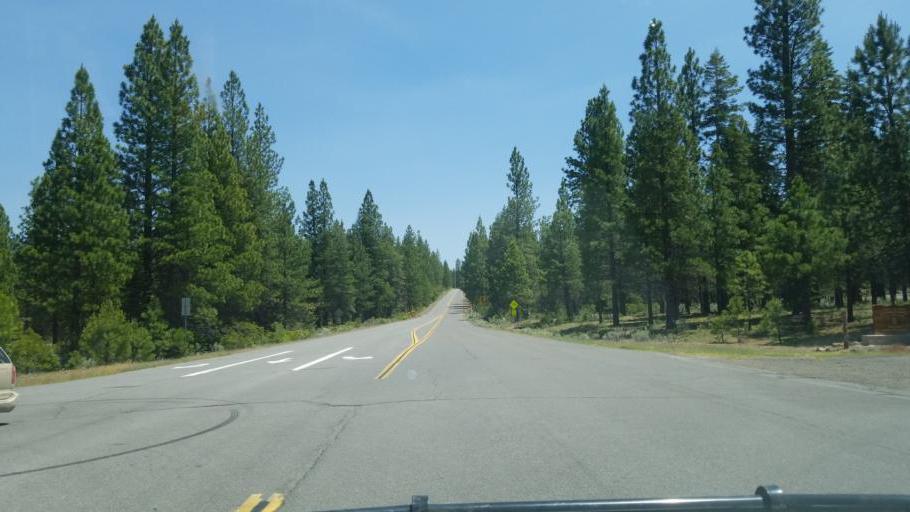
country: US
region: California
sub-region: Lassen County
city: Susanville
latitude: 40.5428
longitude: -120.7963
